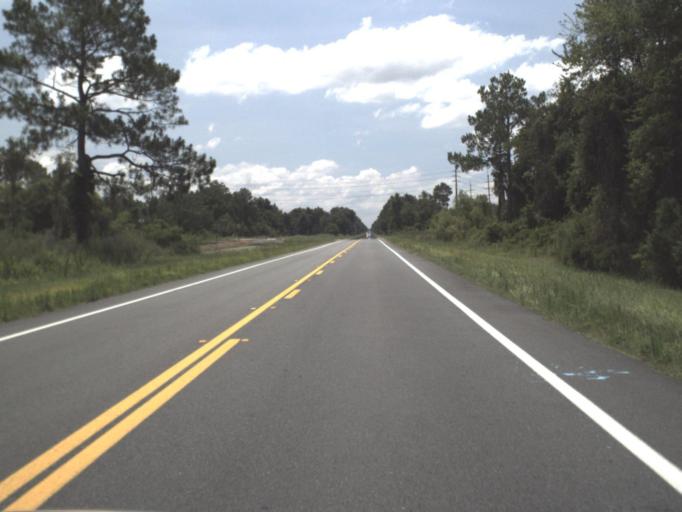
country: US
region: Florida
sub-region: Hamilton County
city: Jasper
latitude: 30.4345
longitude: -82.8702
